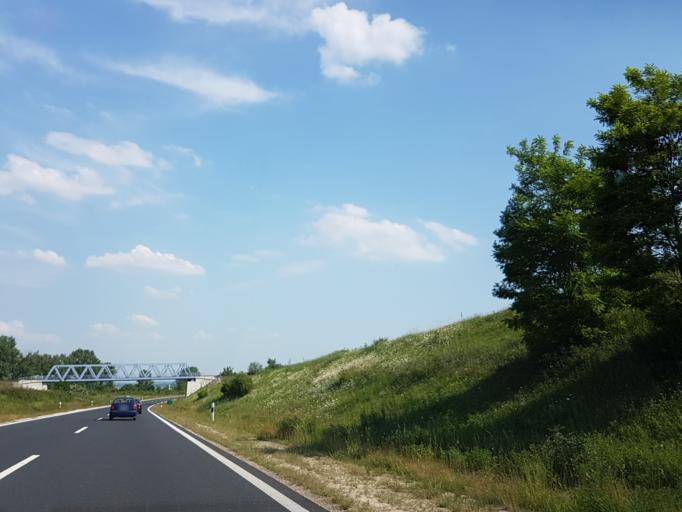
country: HU
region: Veszprem
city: Balatonkenese
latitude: 47.0259
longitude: 18.1781
